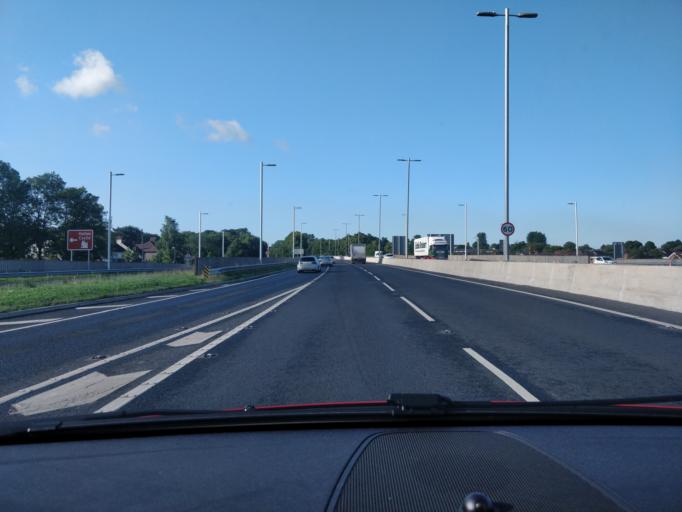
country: GB
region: England
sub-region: Borough of Halton
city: Halton
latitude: 53.3390
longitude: -2.7031
